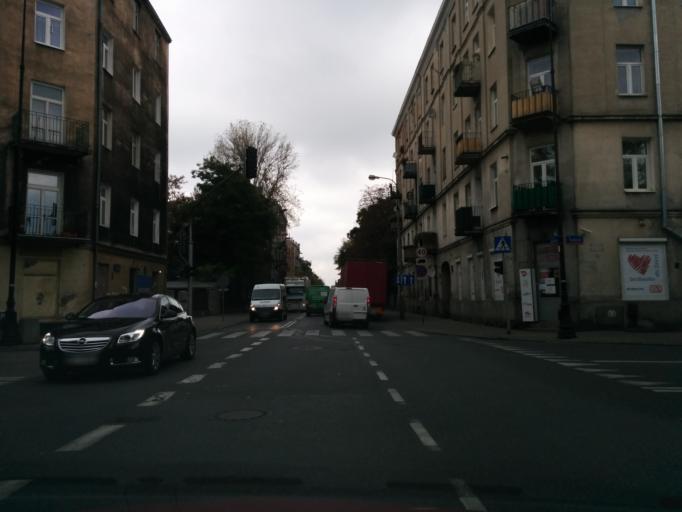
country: PL
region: Masovian Voivodeship
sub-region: Warszawa
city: Praga Polnoc
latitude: 52.2619
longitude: 21.0453
